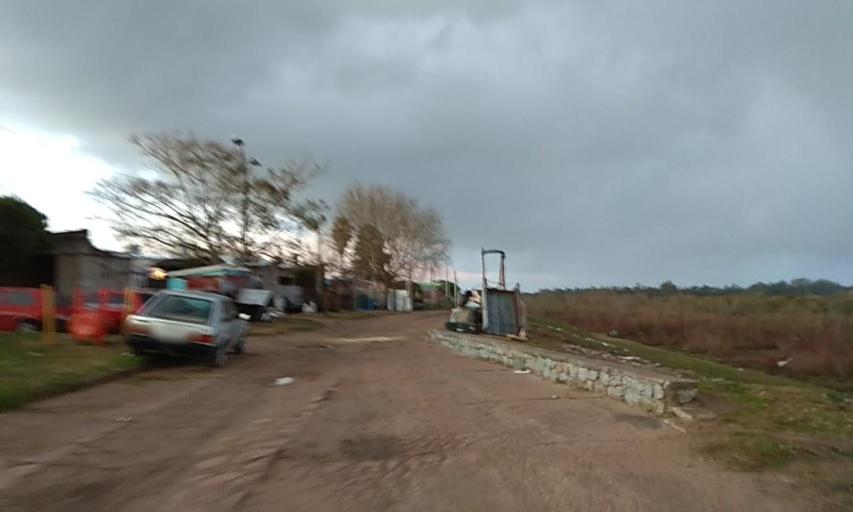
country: UY
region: Florida
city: Florida
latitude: -34.1100
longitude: -56.2084
